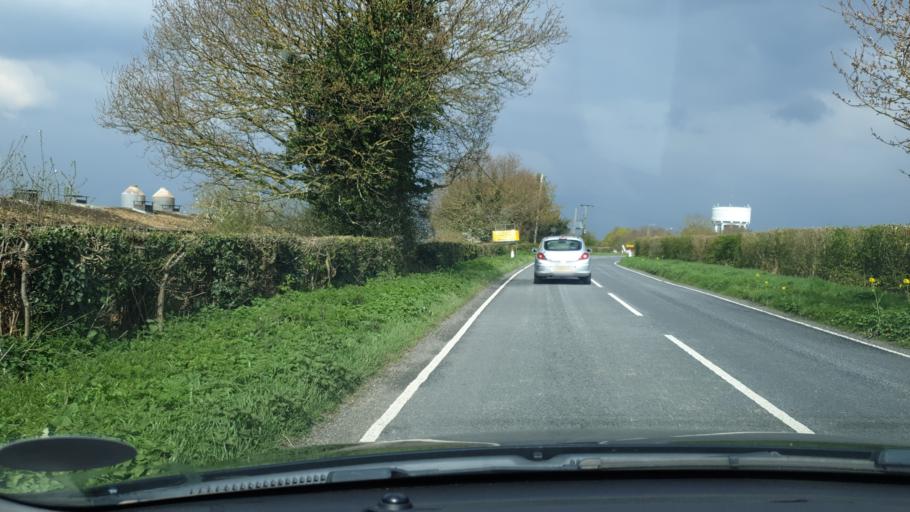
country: GB
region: England
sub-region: Essex
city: Mistley
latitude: 51.9014
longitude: 1.0879
